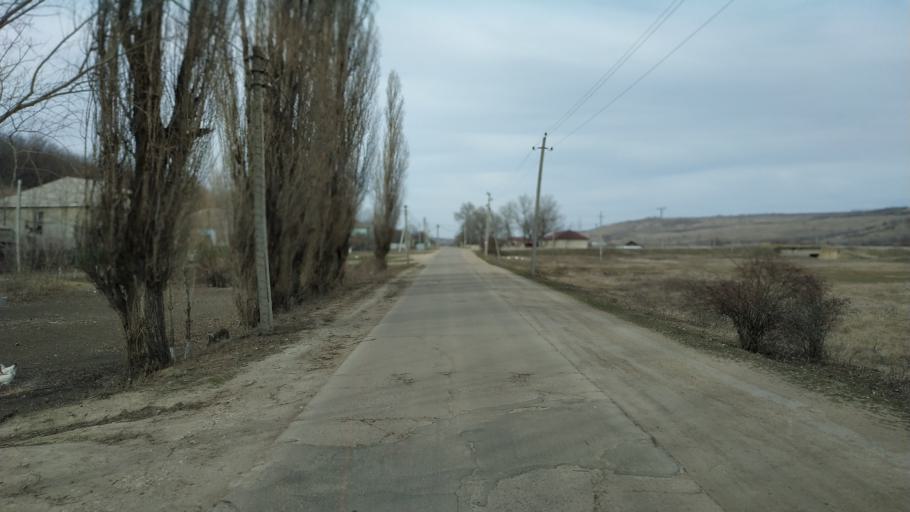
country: RO
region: Vaslui
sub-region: Comuna Dranceni
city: Dranceni
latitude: 46.8704
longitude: 28.1988
